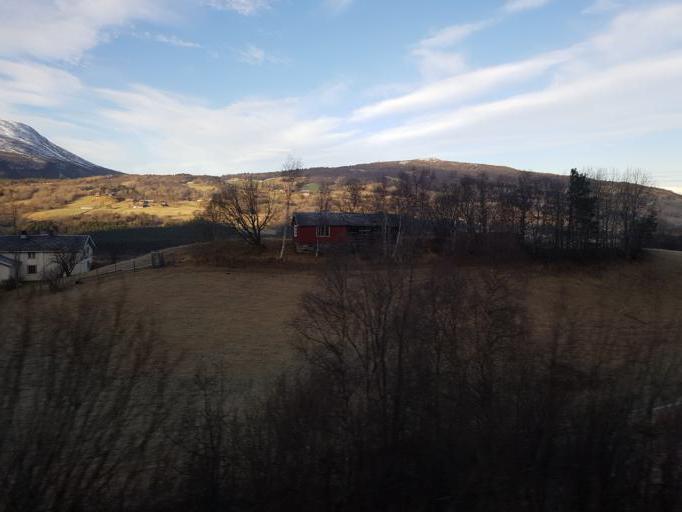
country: NO
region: Sor-Trondelag
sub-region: Oppdal
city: Oppdal
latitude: 62.5320
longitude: 9.6170
